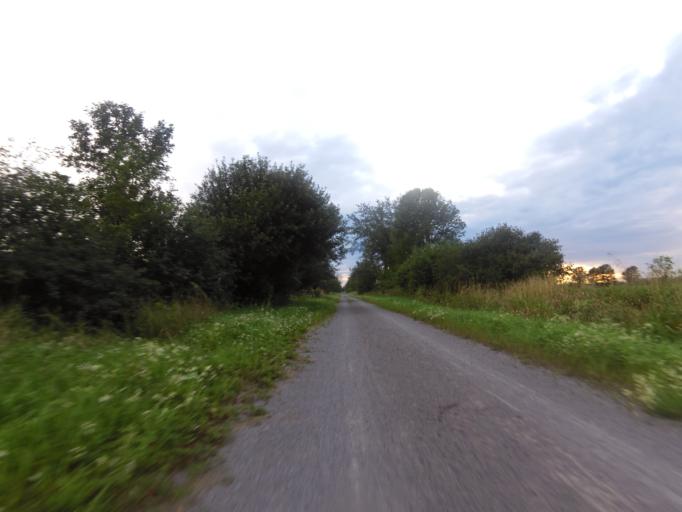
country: CA
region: Ontario
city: Carleton Place
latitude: 45.1561
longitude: -76.0900
